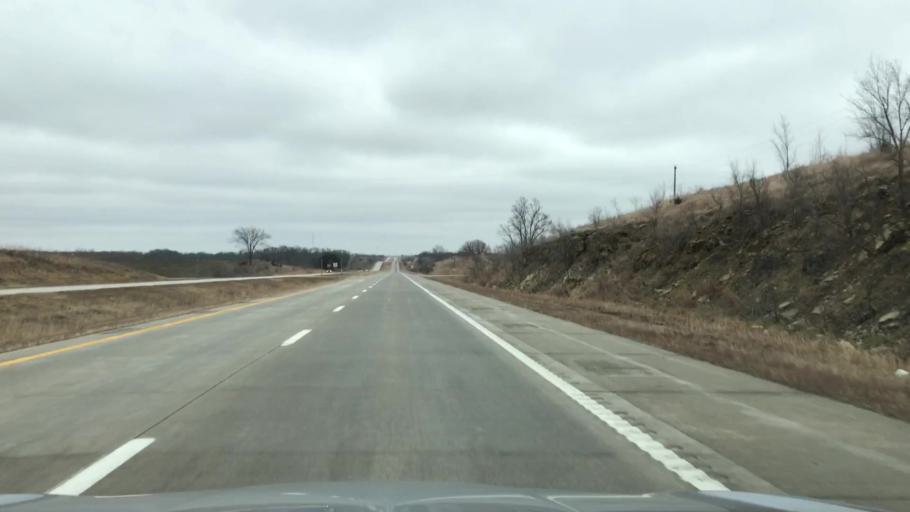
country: US
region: Missouri
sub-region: Caldwell County
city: Hamilton
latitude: 39.7350
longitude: -93.8351
